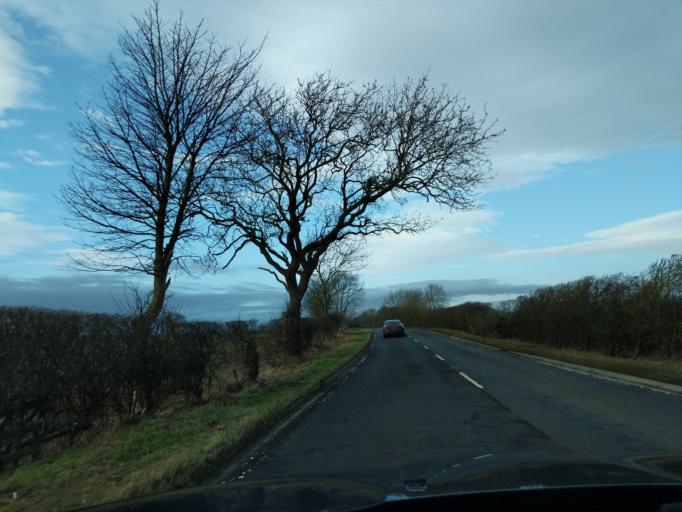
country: GB
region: England
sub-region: Northumberland
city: Darras Hall
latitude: 55.0671
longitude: -1.7852
